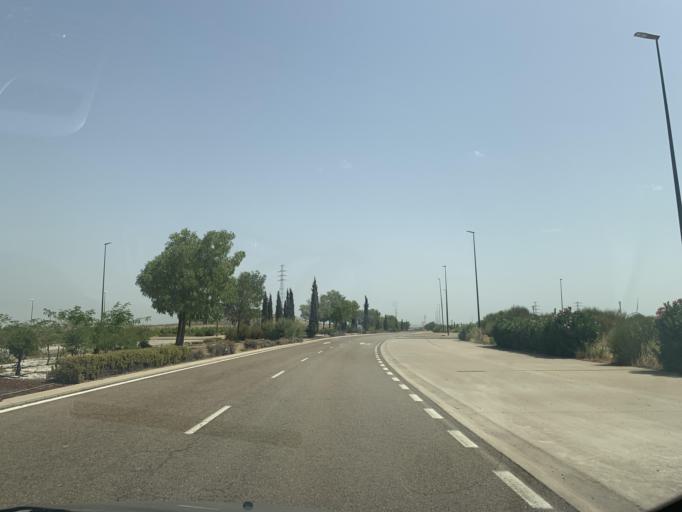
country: ES
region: Aragon
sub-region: Provincia de Zaragoza
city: Zaragoza
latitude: 41.5881
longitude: -0.8362
